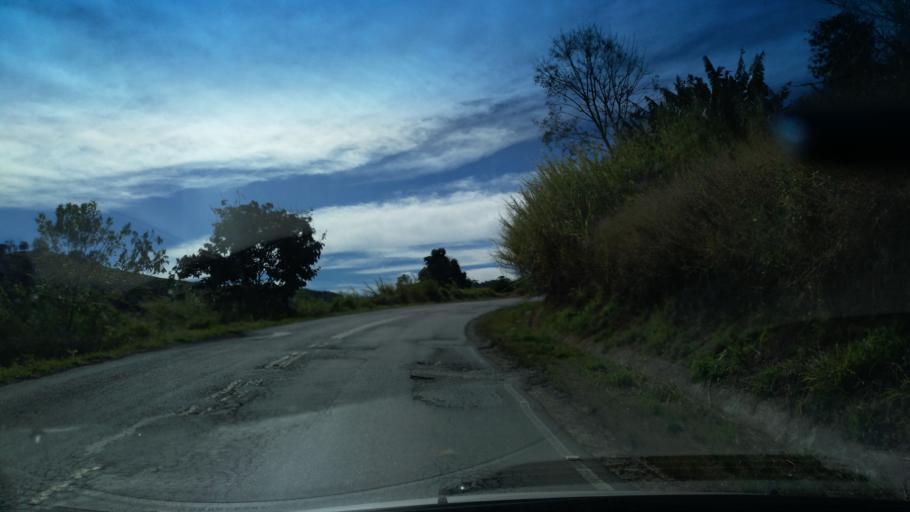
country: BR
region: Minas Gerais
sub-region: Andradas
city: Andradas
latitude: -22.0603
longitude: -46.3731
